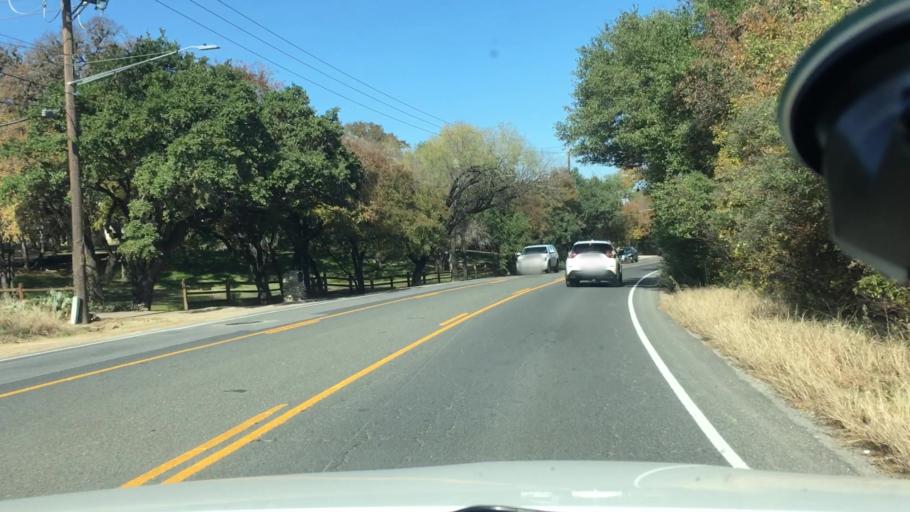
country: US
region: Texas
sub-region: Bexar County
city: Hollywood Park
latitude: 29.5843
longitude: -98.4231
